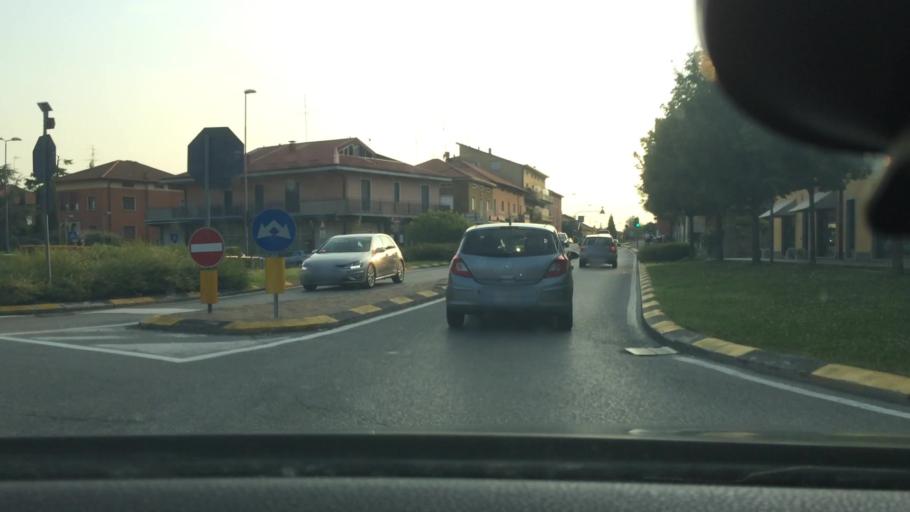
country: IT
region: Lombardy
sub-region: Provincia di Bergamo
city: Curno
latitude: 45.6935
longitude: 9.6119
